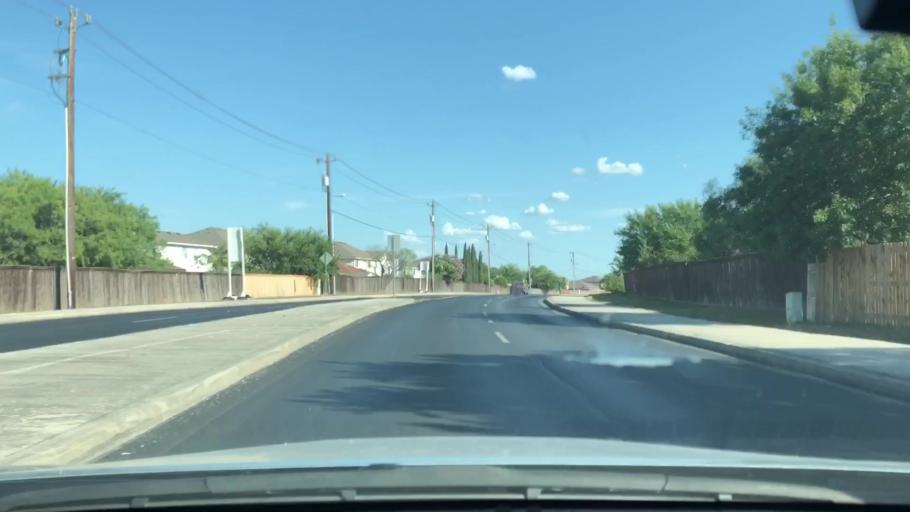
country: US
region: Texas
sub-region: Bexar County
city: Kirby
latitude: 29.4768
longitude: -98.3468
